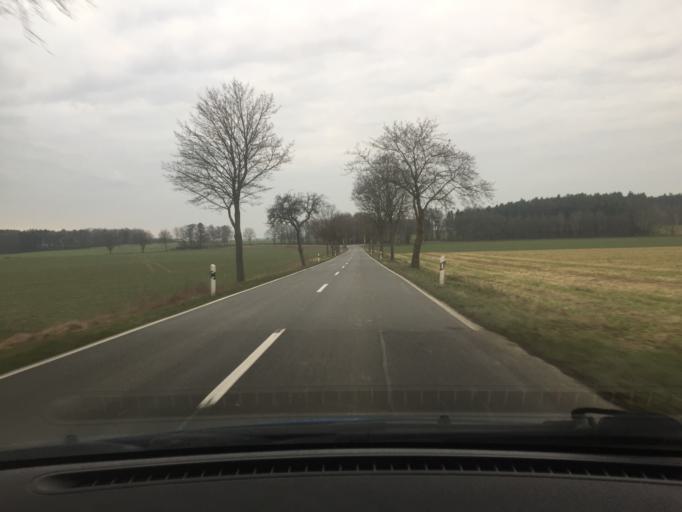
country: DE
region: Lower Saxony
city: Oetzen
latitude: 53.0344
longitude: 10.6686
